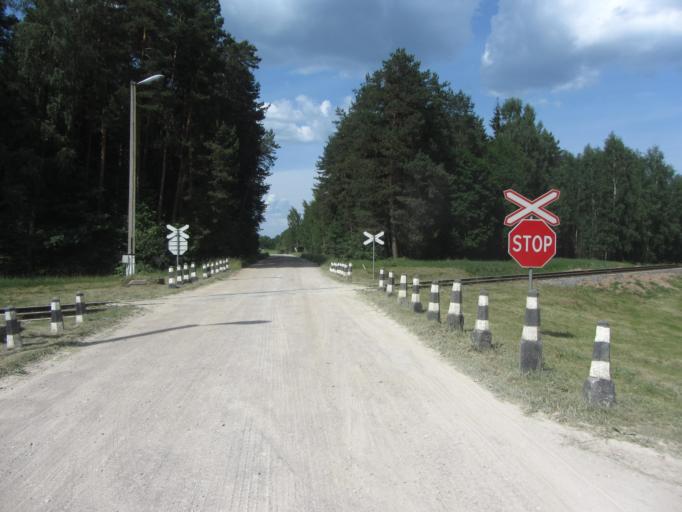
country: LT
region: Kauno apskritis
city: Jonava
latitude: 55.1133
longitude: 24.3214
